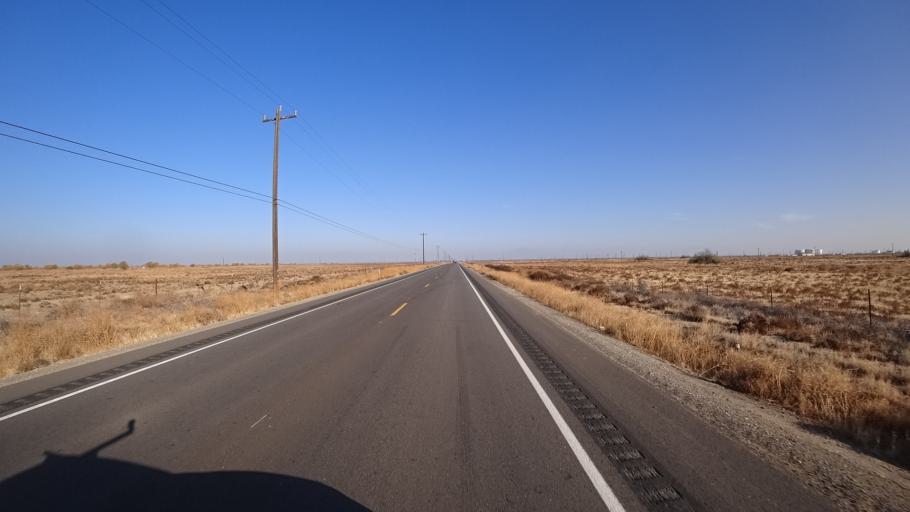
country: US
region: California
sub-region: Kern County
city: Rosedale
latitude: 35.2961
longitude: -119.2211
